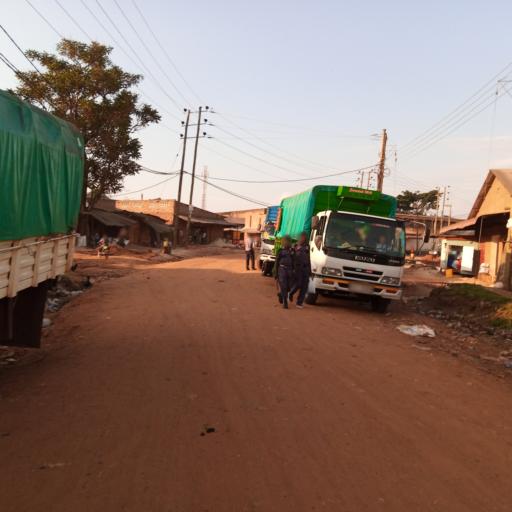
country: UG
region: Eastern Region
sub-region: Mbale District
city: Mbale
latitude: 1.0768
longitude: 34.1626
